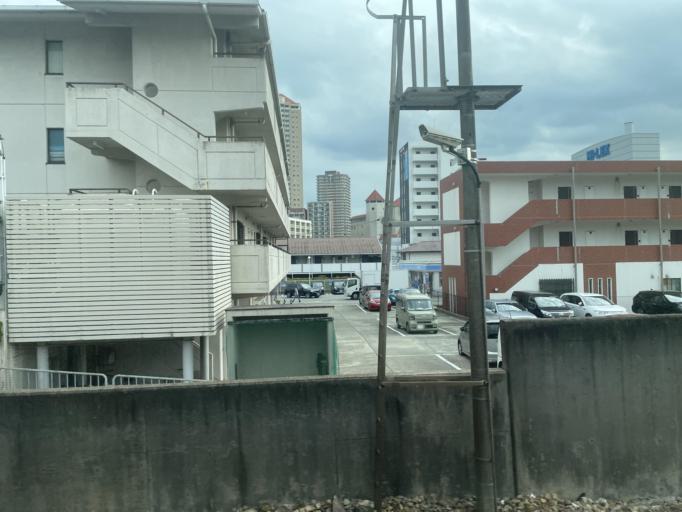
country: JP
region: Hyogo
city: Takarazuka
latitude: 34.8101
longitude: 135.3475
